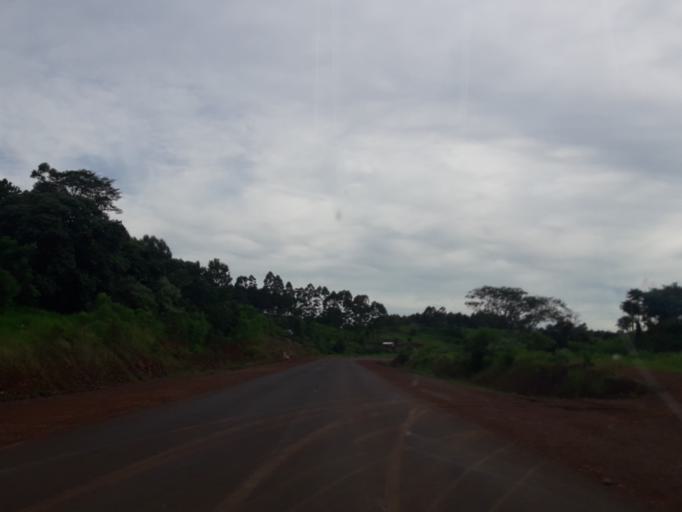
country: AR
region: Misiones
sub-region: Departamento de San Pedro
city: San Pedro
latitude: -26.5161
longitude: -53.9349
